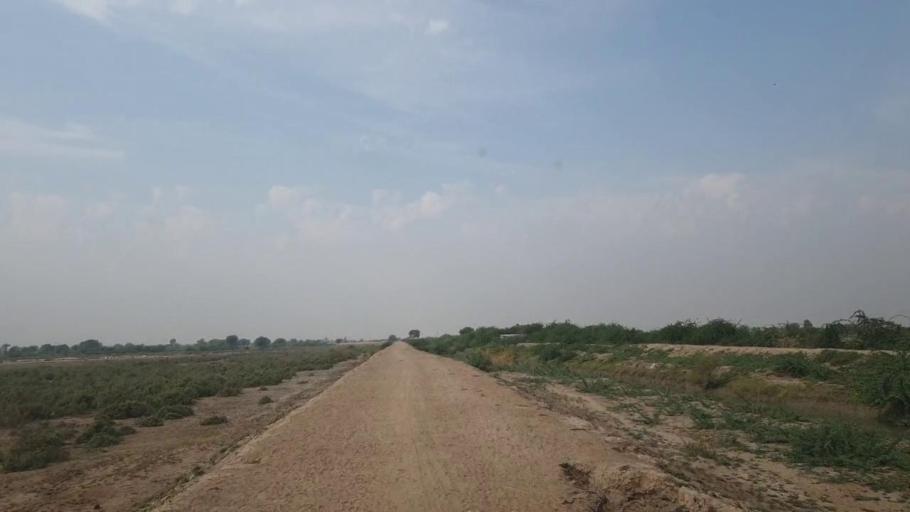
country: PK
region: Sindh
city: Rajo Khanani
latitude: 24.9649
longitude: 69.0148
